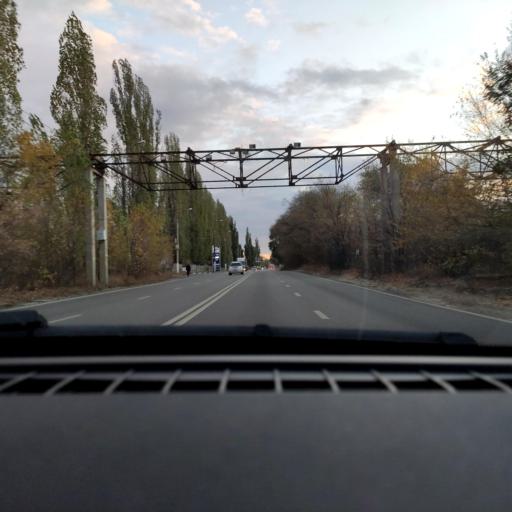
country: RU
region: Voronezj
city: Maslovka
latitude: 51.6033
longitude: 39.2539
